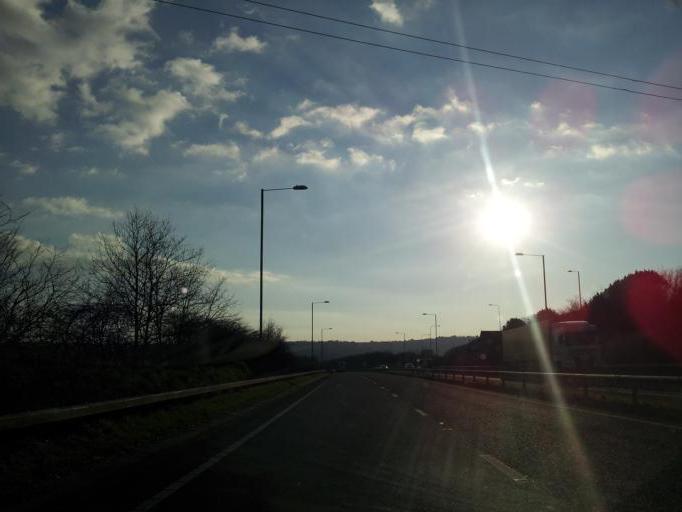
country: GB
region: England
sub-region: Cornwall
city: Launceston
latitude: 50.6432
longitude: -4.3092
